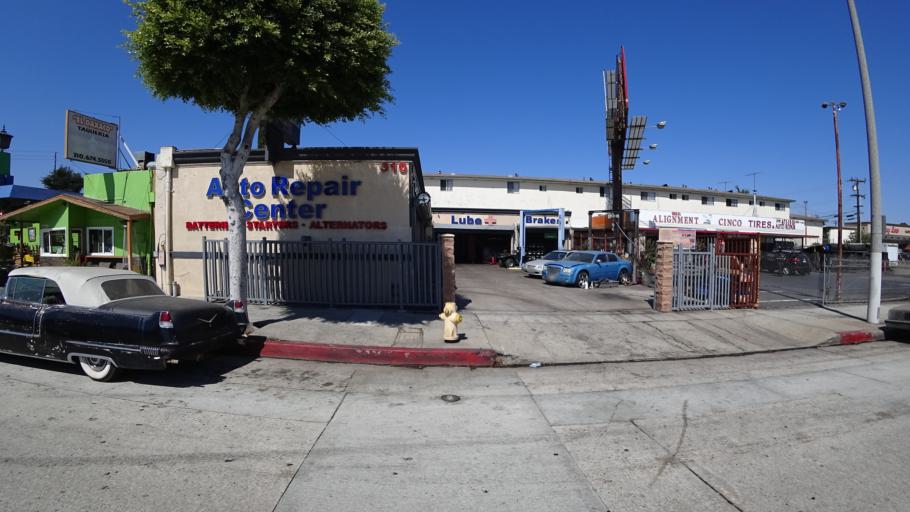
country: US
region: California
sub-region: Los Angeles County
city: Inglewood
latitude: 33.9672
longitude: -118.3541
